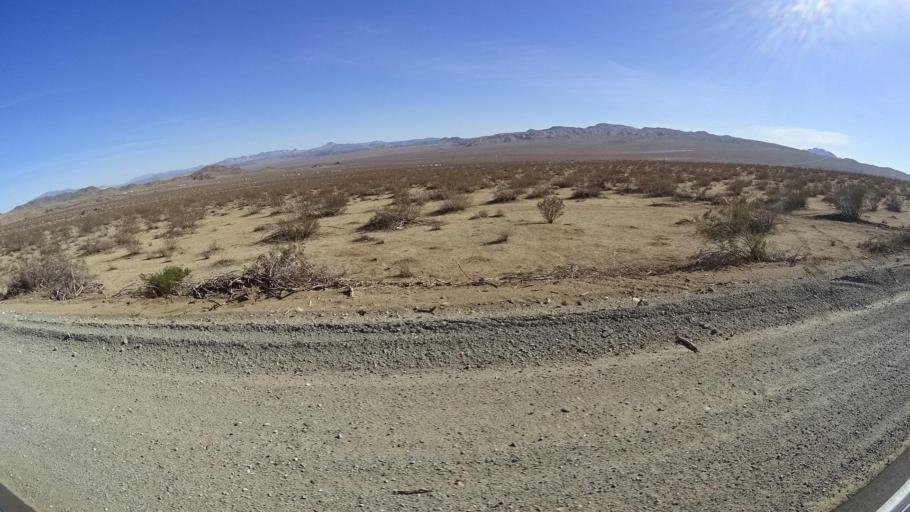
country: US
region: California
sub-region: Kern County
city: Ridgecrest
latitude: 35.5331
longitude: -117.5908
